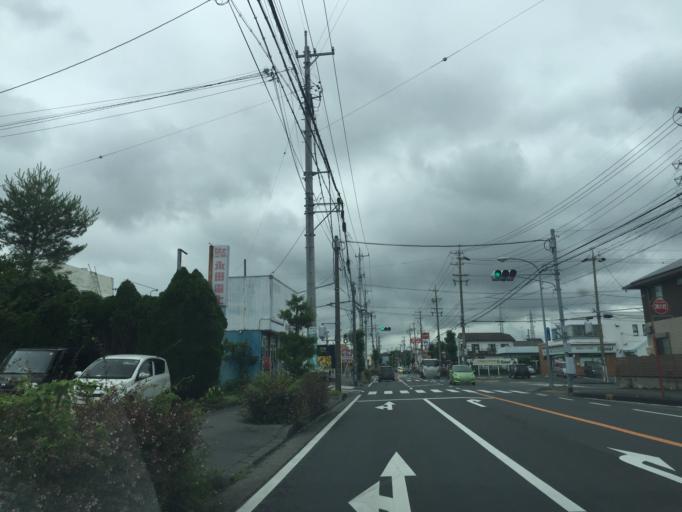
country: JP
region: Shizuoka
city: Fukuroi
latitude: 34.7597
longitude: 137.9178
